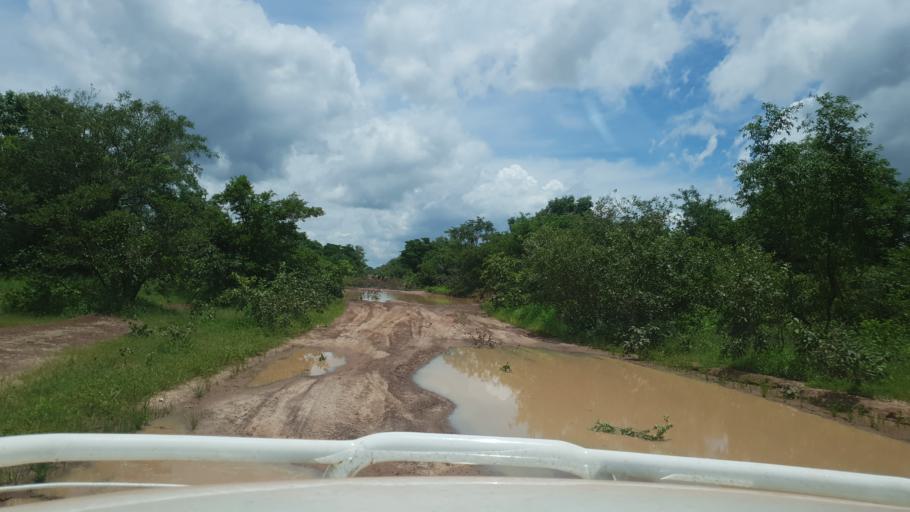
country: ML
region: Koulikoro
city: Banamba
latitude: 13.2000
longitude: -7.3320
